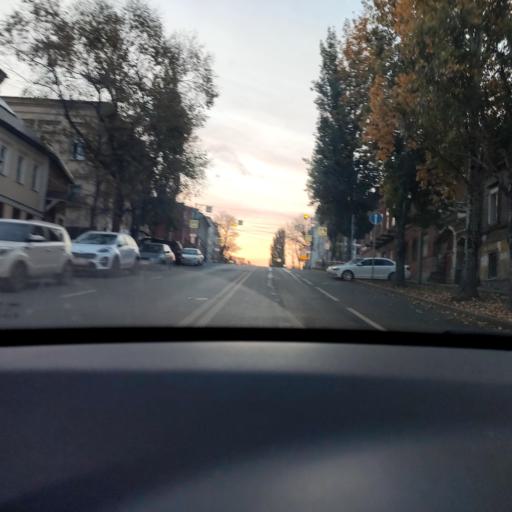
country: RU
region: Samara
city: Rozhdestveno
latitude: 53.1863
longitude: 50.0844
